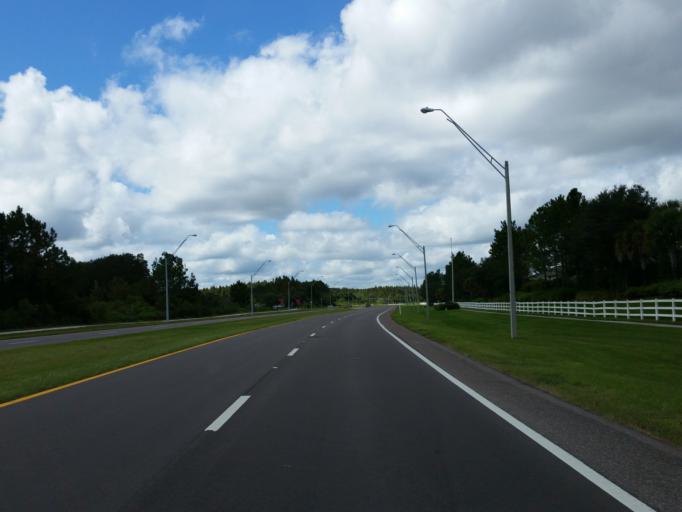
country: US
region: Florida
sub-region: Hillsborough County
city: Pebble Creek
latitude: 28.1438
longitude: -82.2928
